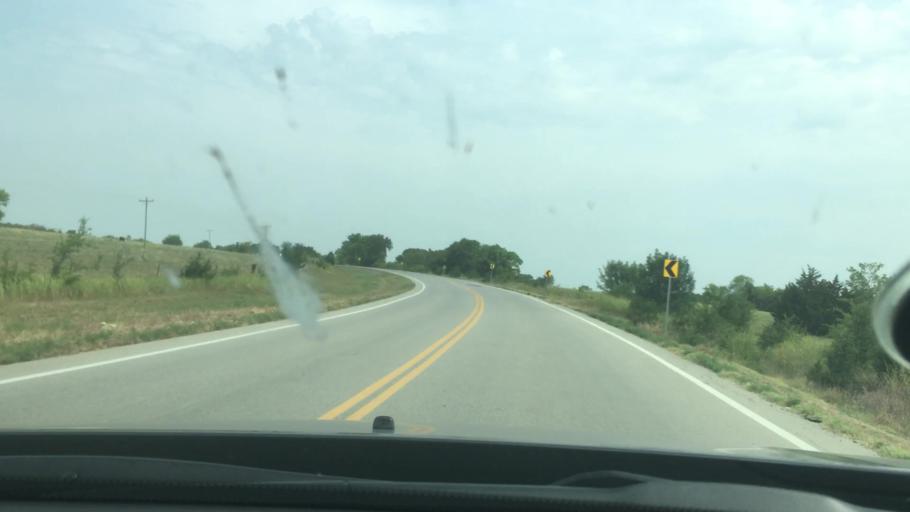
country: US
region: Oklahoma
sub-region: Bryan County
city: Durant
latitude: 34.1460
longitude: -96.3736
